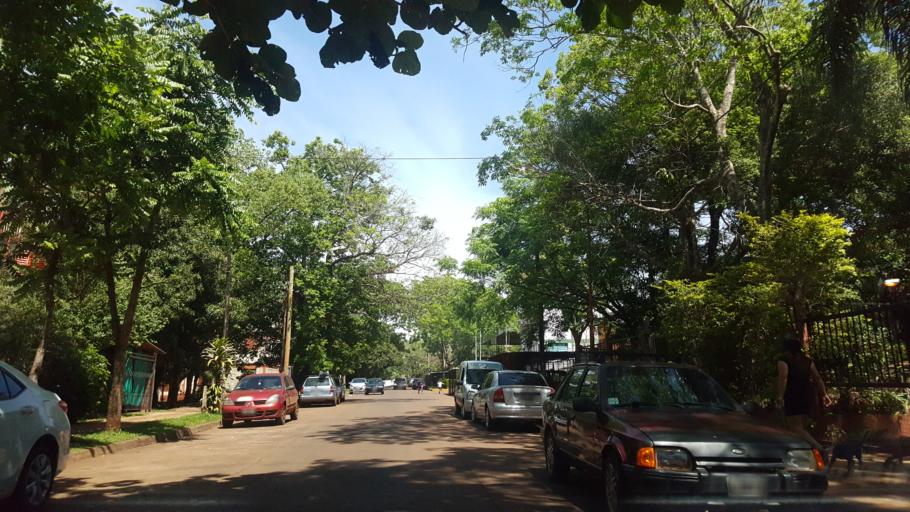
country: AR
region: Misiones
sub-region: Departamento de Capital
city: Posadas
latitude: -27.3954
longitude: -55.9064
